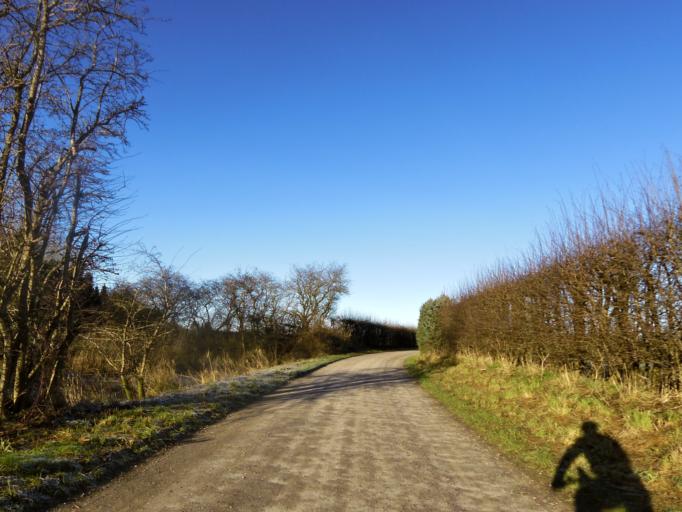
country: DK
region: South Denmark
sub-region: Tonder Kommune
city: Sherrebek
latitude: 55.1640
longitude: 8.7651
